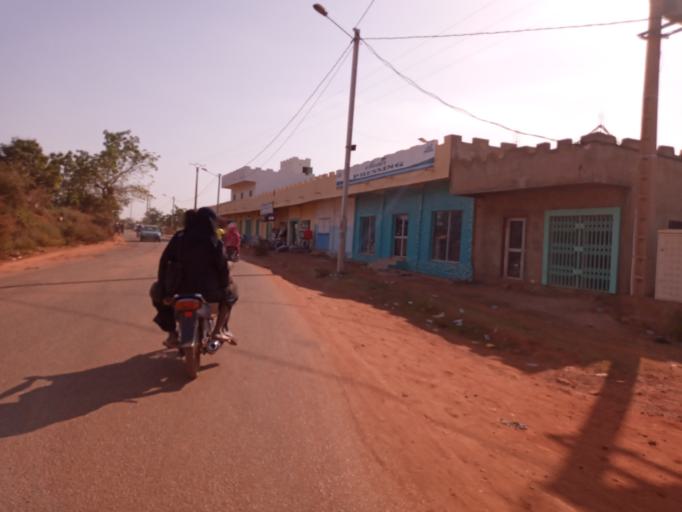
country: ML
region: Bamako
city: Bamako
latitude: 12.6264
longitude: -7.9552
